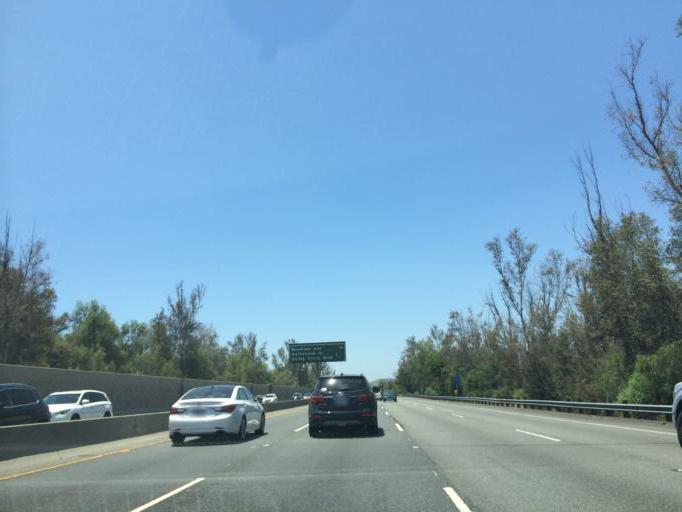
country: US
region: California
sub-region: Los Angeles County
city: Woodland Hills
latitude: 34.1658
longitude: -118.6197
